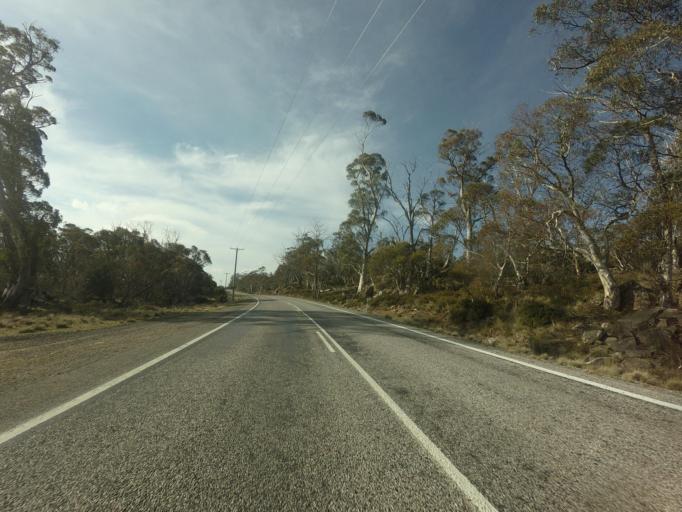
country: AU
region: Tasmania
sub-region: Meander Valley
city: Deloraine
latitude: -41.9919
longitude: 146.7078
